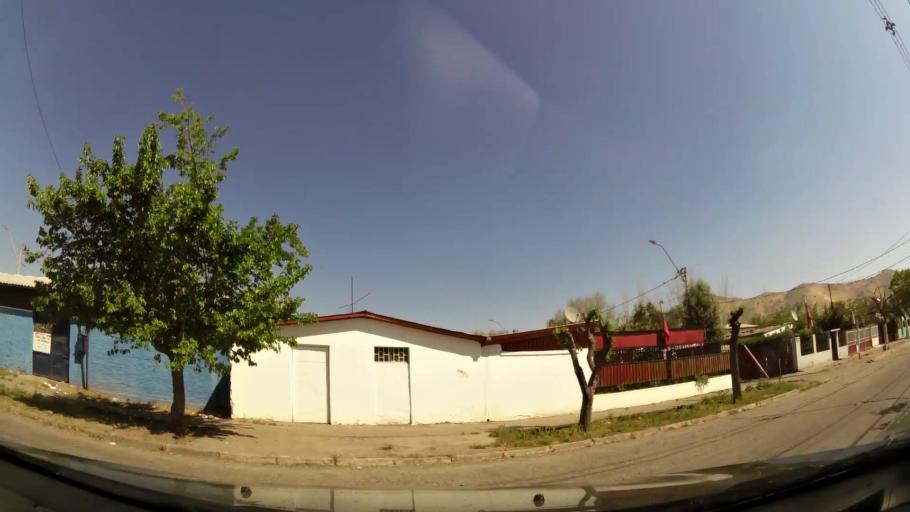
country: CL
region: Santiago Metropolitan
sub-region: Provincia de Maipo
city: San Bernardo
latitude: -33.5846
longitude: -70.7079
